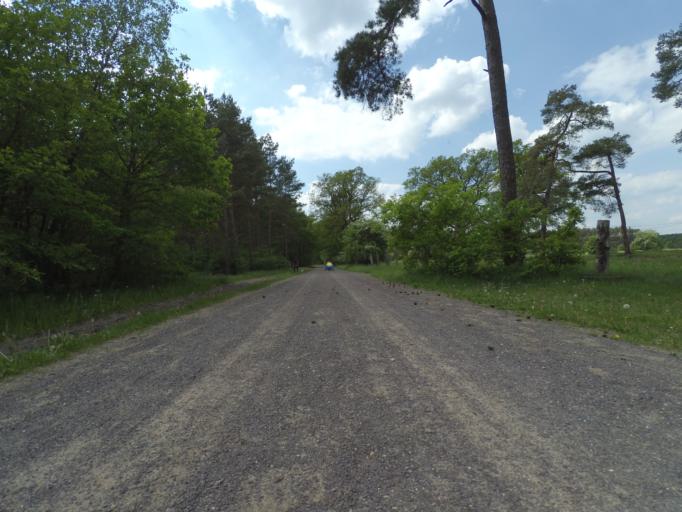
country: DE
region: Lower Saxony
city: Winsen (Aller)
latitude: 52.6734
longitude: 9.8910
